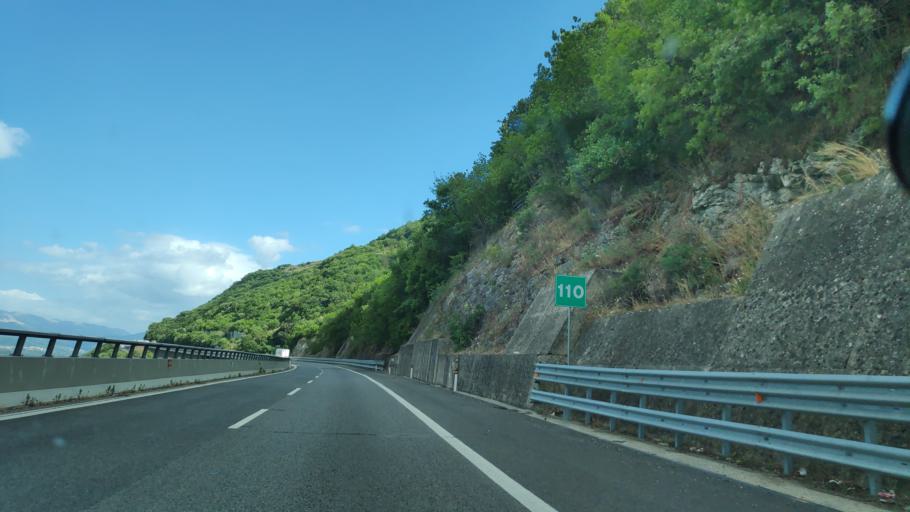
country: IT
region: Campania
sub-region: Provincia di Salerno
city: Sicignano degli Alburni
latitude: 40.5940
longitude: 15.3234
